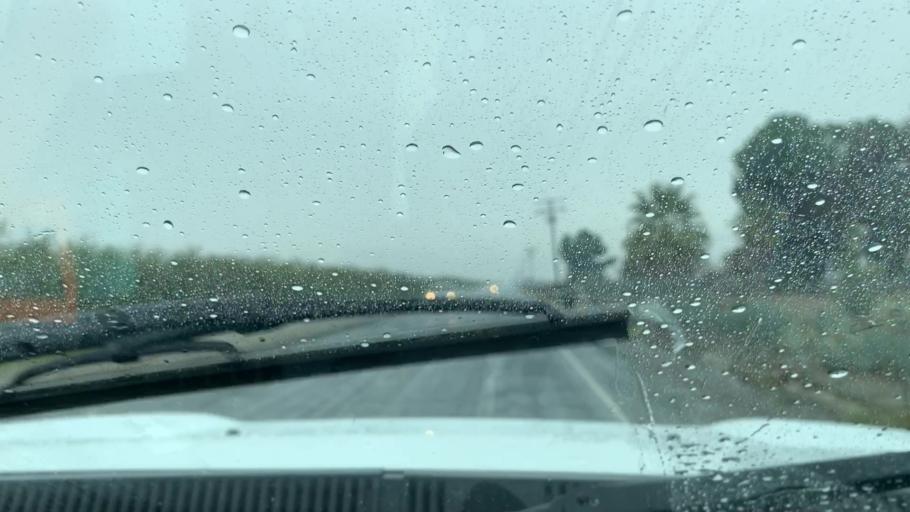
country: US
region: California
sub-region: Tulare County
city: Earlimart
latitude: 35.8919
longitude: -119.3289
